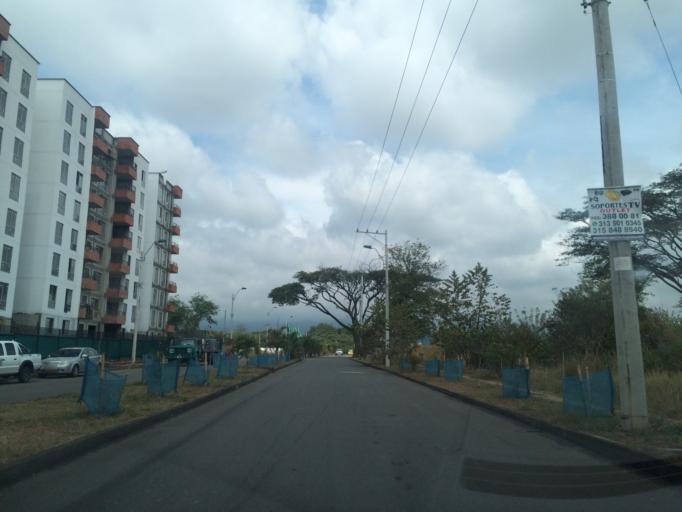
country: CO
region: Valle del Cauca
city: Cali
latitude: 3.3563
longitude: -76.5205
